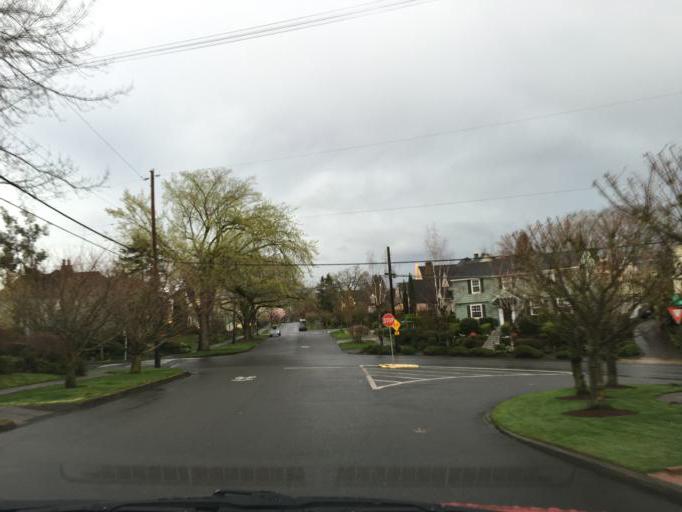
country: US
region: Oregon
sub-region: Multnomah County
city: Portland
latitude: 45.5454
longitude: -122.6215
